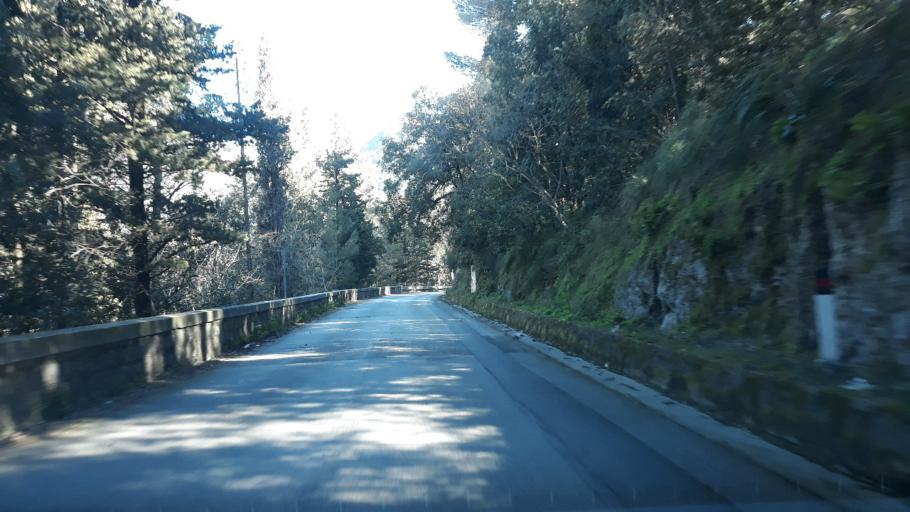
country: IT
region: Sicily
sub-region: Palermo
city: Piano dei Geli
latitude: 38.0924
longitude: 13.2543
